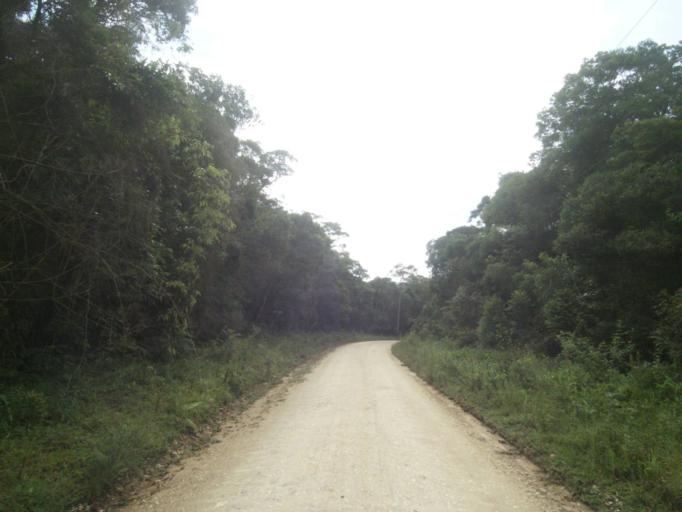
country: BR
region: Parana
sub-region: Campina Grande Do Sul
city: Campina Grande do Sul
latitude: -25.3221
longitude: -49.0679
